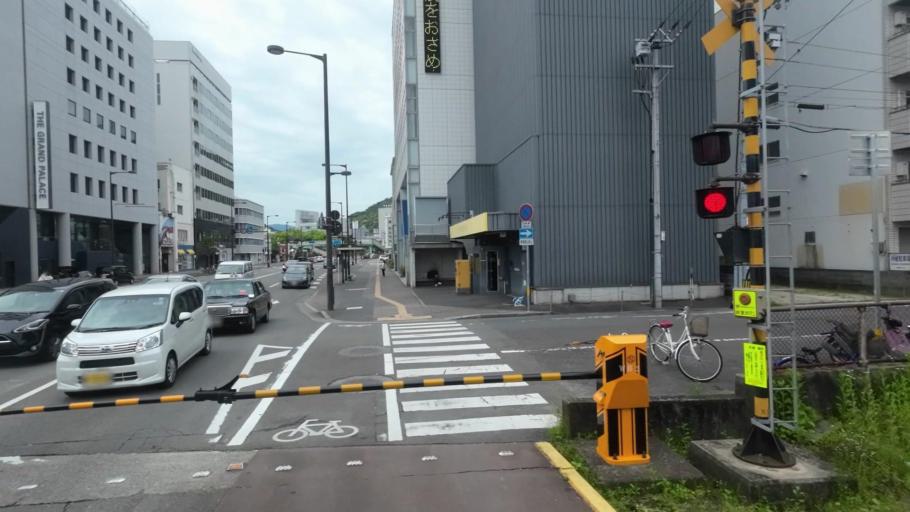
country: JP
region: Tokushima
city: Tokushima-shi
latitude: 34.0758
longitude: 134.5486
